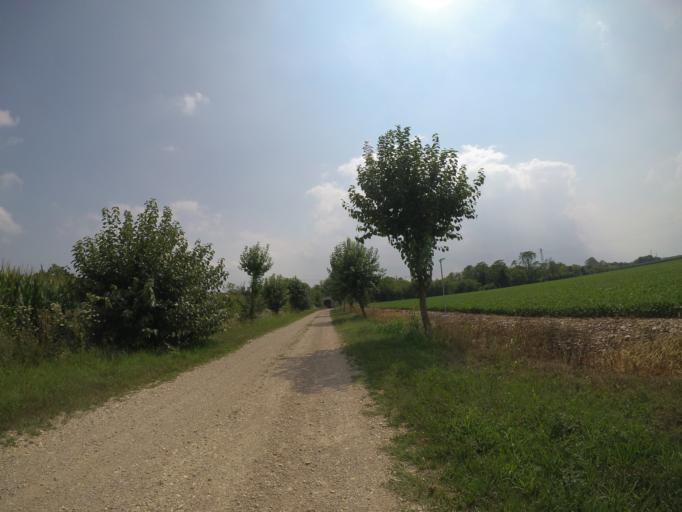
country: IT
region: Friuli Venezia Giulia
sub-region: Provincia di Udine
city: Codroipo
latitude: 45.9790
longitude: 13.0109
